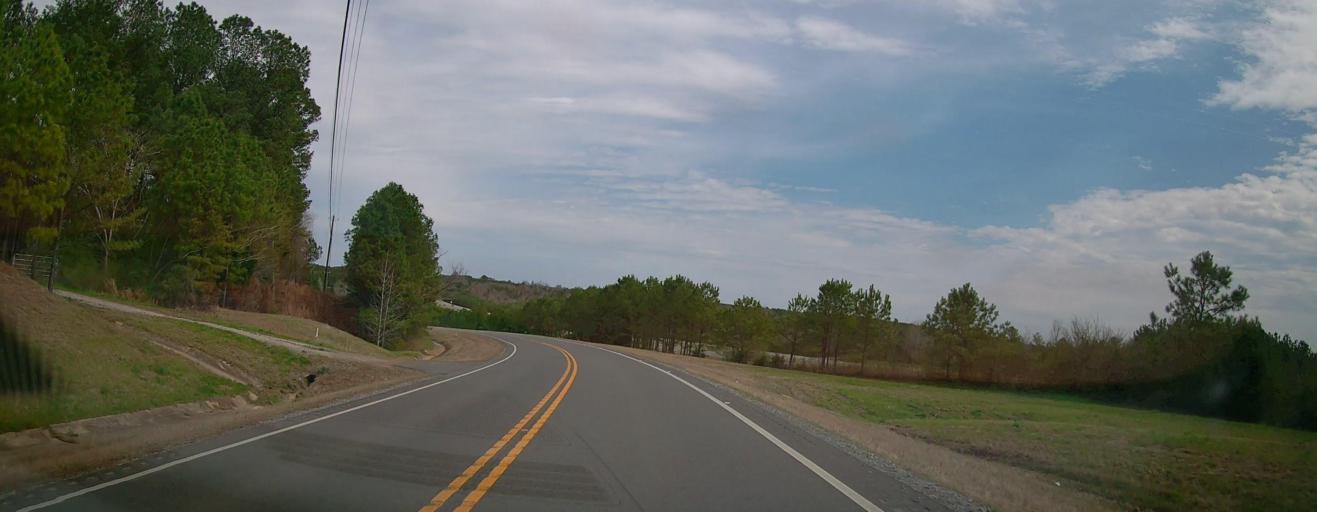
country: US
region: Alabama
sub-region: Walker County
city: Carbon Hill
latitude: 33.8648
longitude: -87.4088
